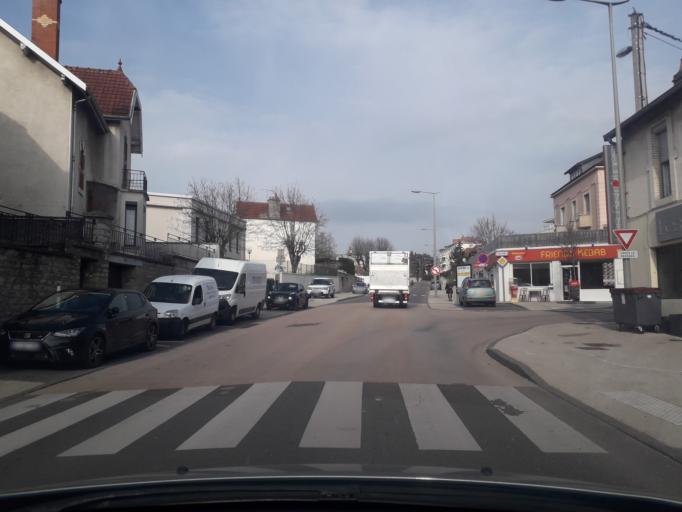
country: FR
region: Bourgogne
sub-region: Departement de la Cote-d'Or
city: Talant
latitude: 47.3344
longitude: 5.0153
